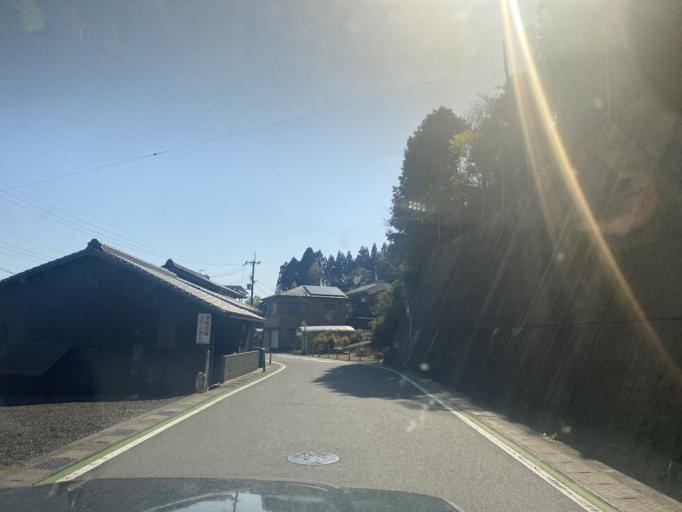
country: JP
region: Kyoto
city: Uji
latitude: 34.8581
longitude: 135.8658
